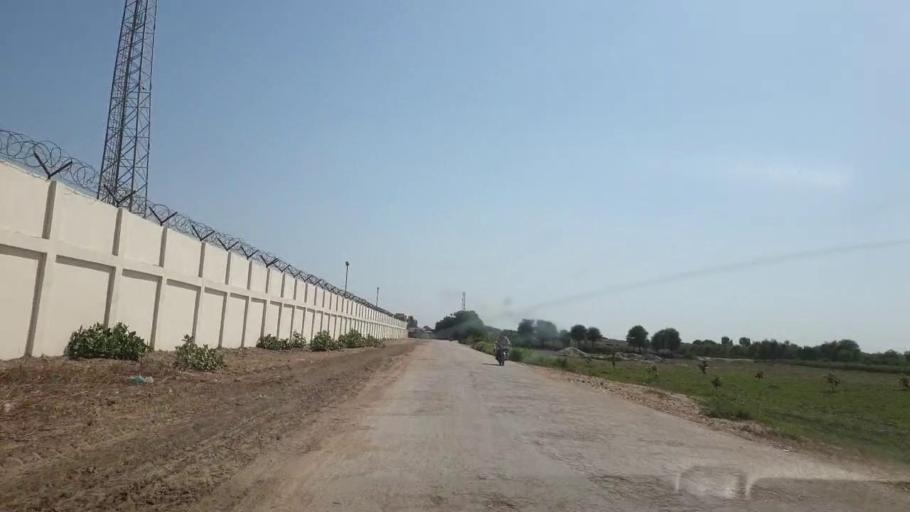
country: PK
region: Sindh
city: Tando Jam
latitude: 25.3852
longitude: 68.5791
